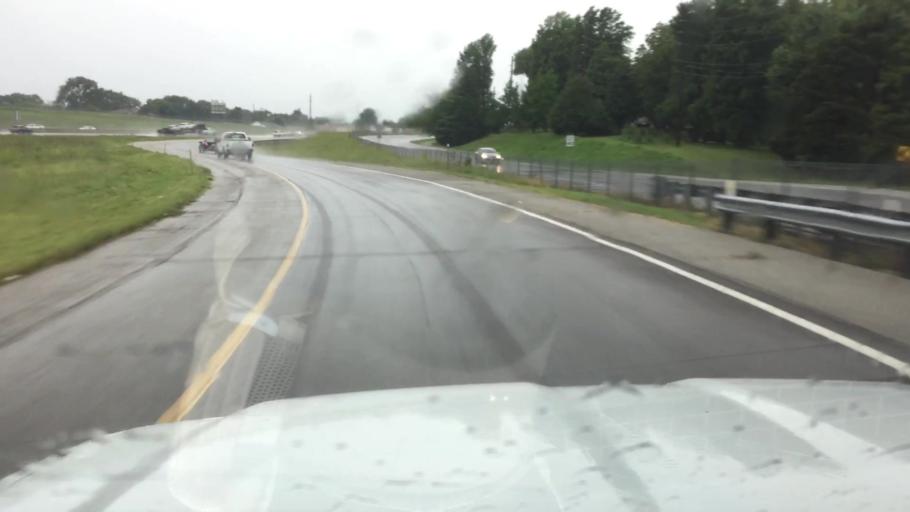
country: US
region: Missouri
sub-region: Saint Louis County
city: Mehlville
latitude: 38.4966
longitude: -90.3030
